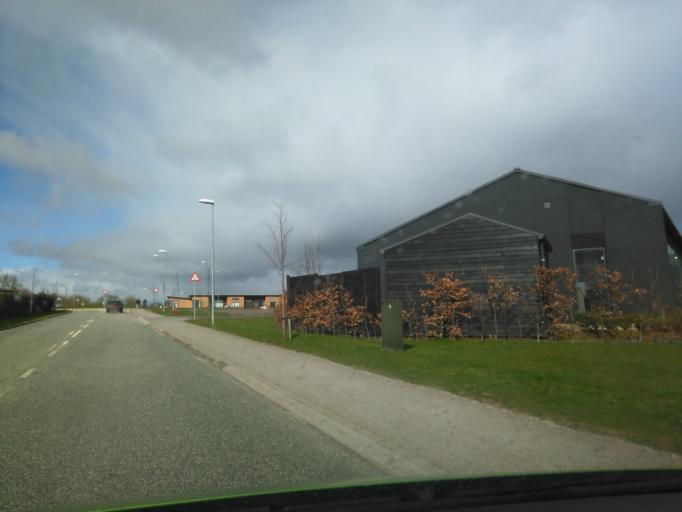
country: DK
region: Central Jutland
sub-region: Arhus Kommune
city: Marslet
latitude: 56.0610
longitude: 10.1570
